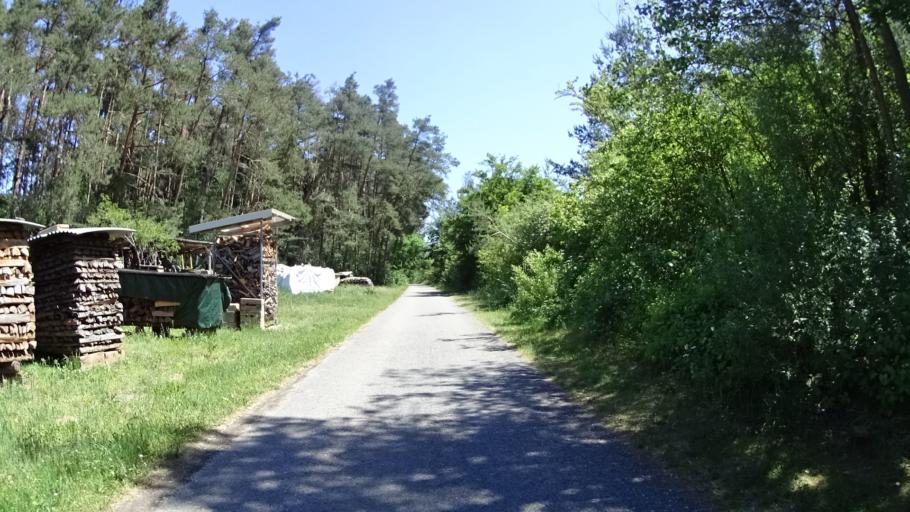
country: DE
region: Bavaria
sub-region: Regierungsbezirk Mittelfranken
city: Pleinfeld
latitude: 49.0949
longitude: 10.9762
